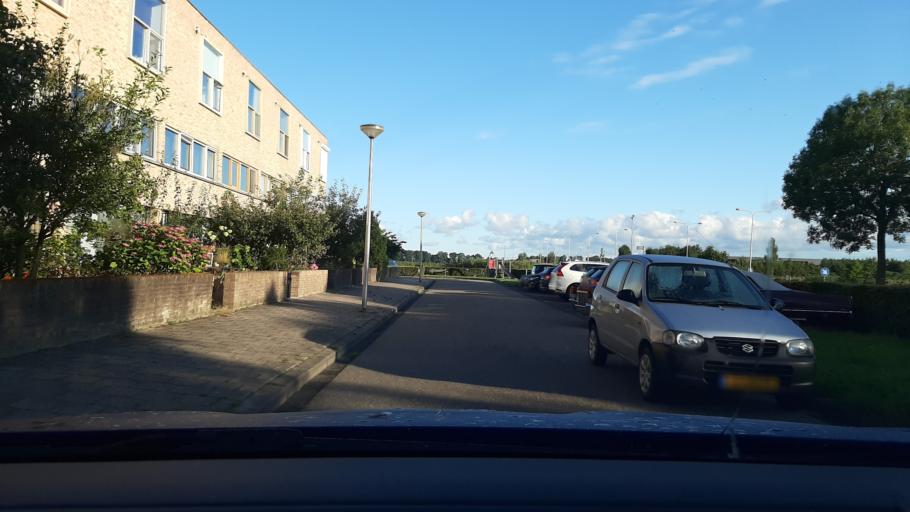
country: NL
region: Flevoland
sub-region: Gemeente Zeewolde
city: Zeewolde
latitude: 52.3441
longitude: 5.5176
